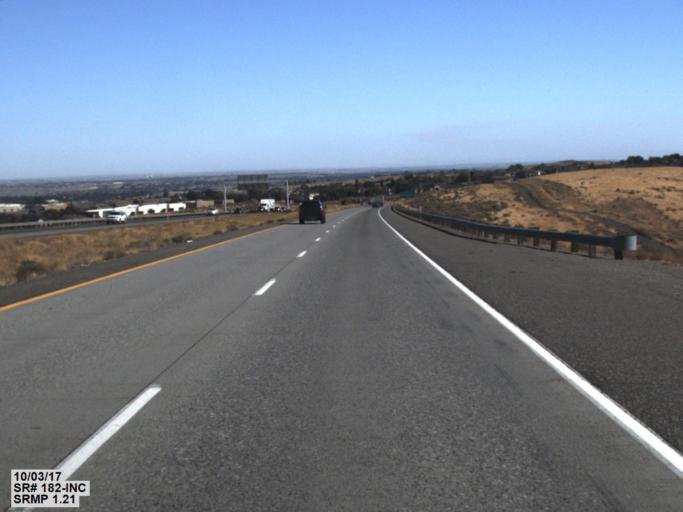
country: US
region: Washington
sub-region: Benton County
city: West Richland
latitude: 46.2464
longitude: -119.3375
